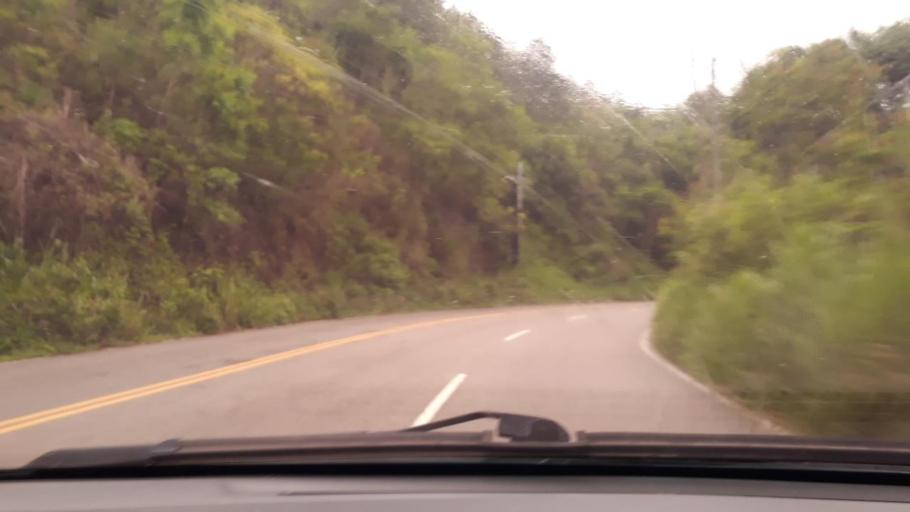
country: GT
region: Chiquimula
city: Esquipulas
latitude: 14.5600
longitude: -89.3658
